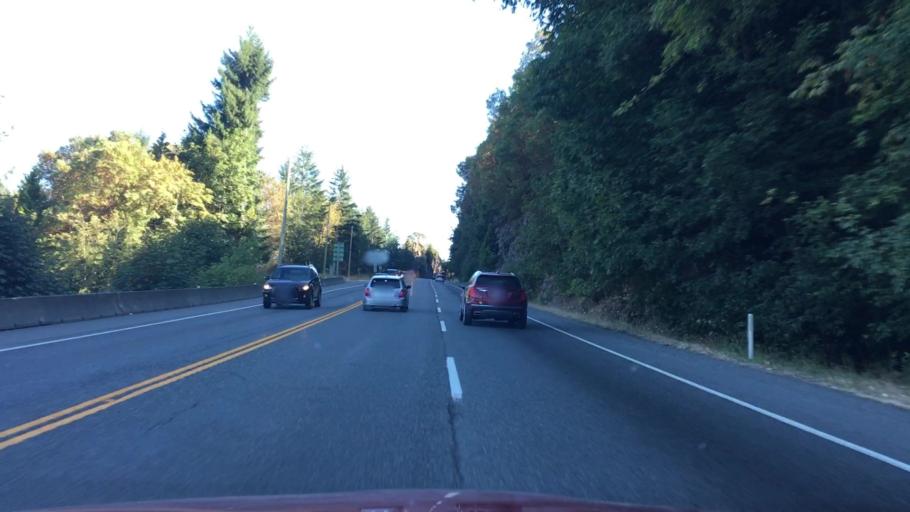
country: CA
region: British Columbia
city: North Saanich
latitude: 48.5882
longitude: -123.5317
